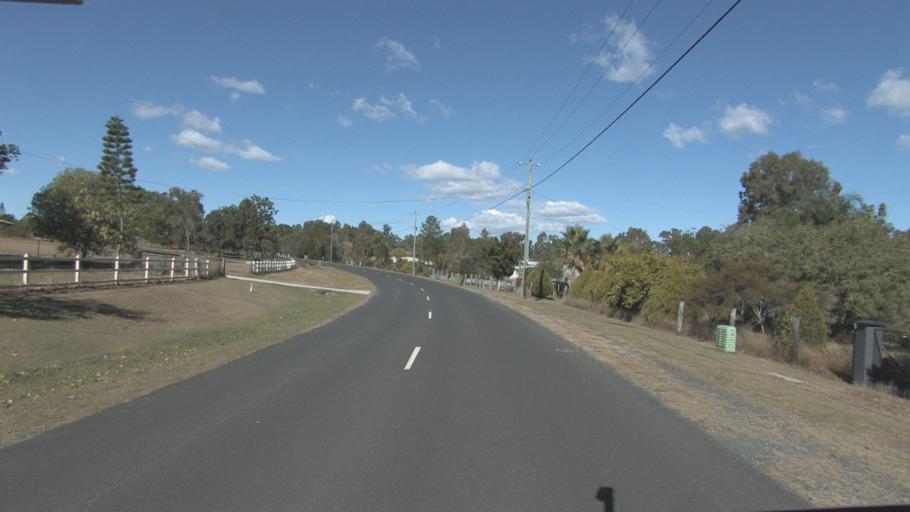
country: AU
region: Queensland
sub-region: Logan
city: North Maclean
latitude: -27.7410
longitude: 152.9462
